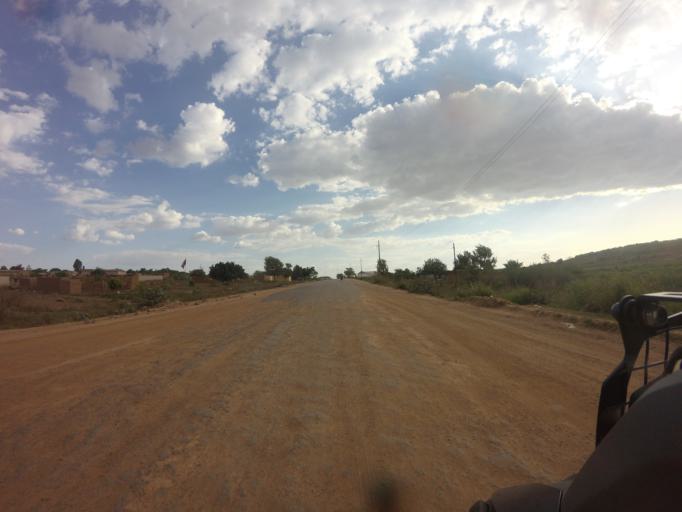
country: AO
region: Huila
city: Lubango
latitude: -14.6676
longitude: 13.8979
